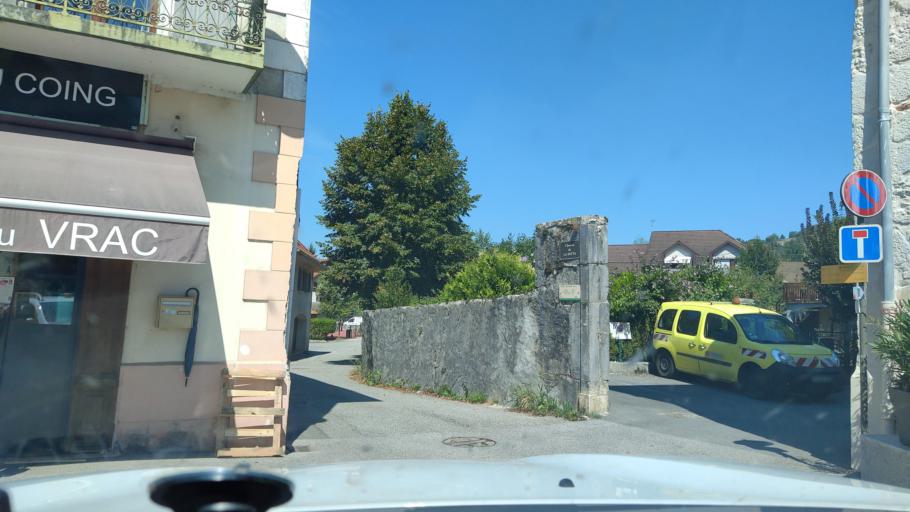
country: FR
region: Rhone-Alpes
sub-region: Departement de la Savoie
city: Novalaise
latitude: 45.5951
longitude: 5.7704
